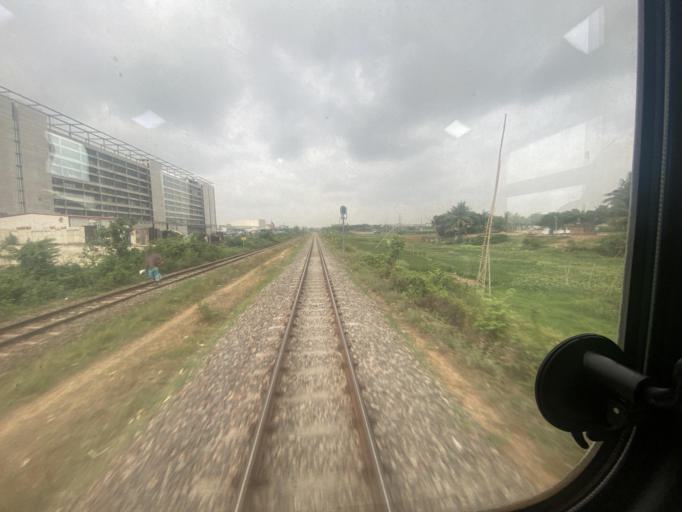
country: BD
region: Dhaka
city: Tungi
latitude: 23.9111
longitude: 90.4166
